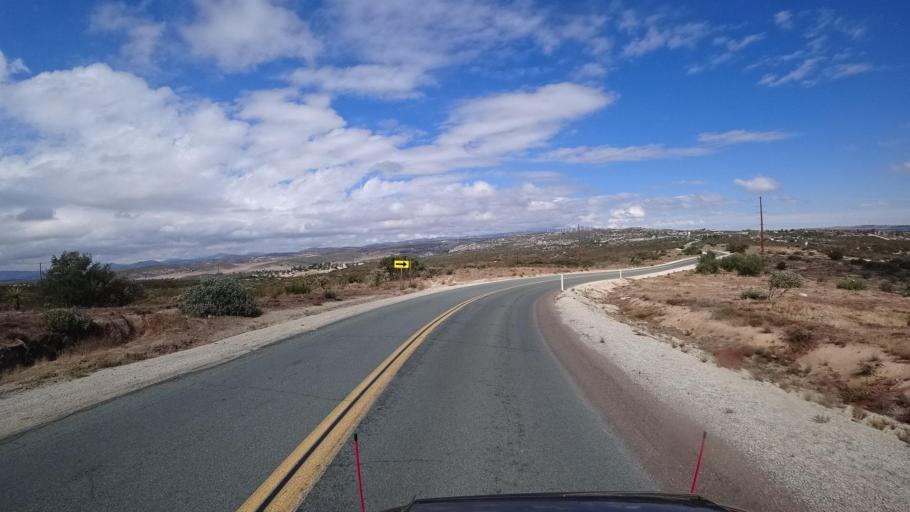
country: US
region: California
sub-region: San Diego County
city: Campo
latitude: 32.6604
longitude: -116.3164
